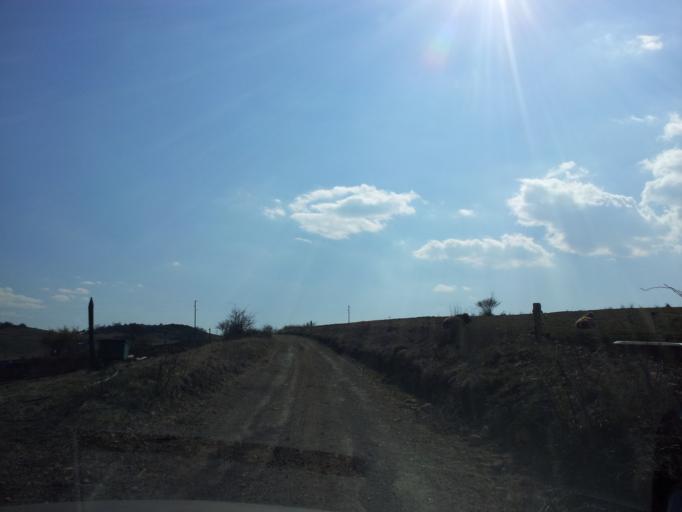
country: HR
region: Zadarska
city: Gracac
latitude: 44.5379
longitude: 15.7472
